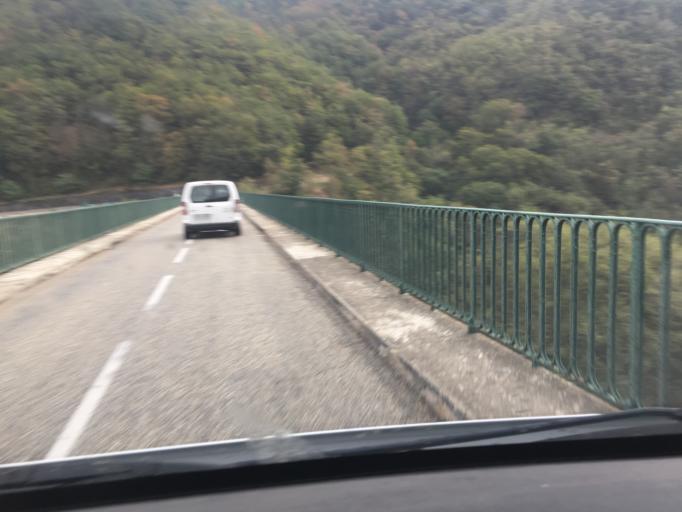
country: FR
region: Rhone-Alpes
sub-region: Departement de l'Ardeche
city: Saint-Jean-de-Muzols
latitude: 45.0568
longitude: 4.7828
